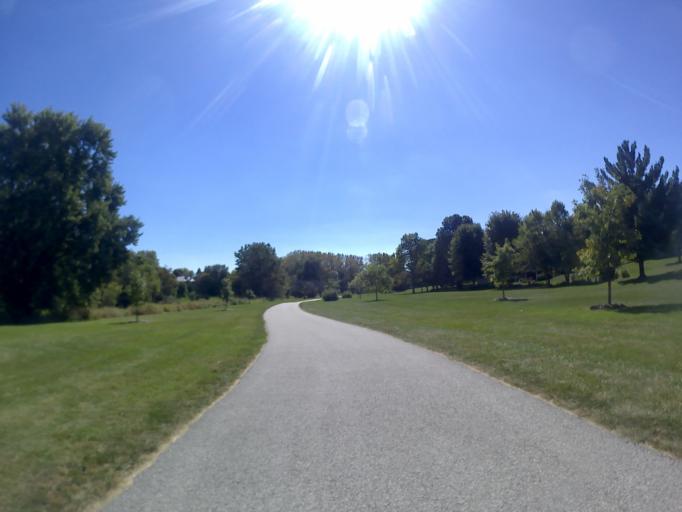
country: US
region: Illinois
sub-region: DuPage County
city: Naperville
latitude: 41.7758
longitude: -88.1685
